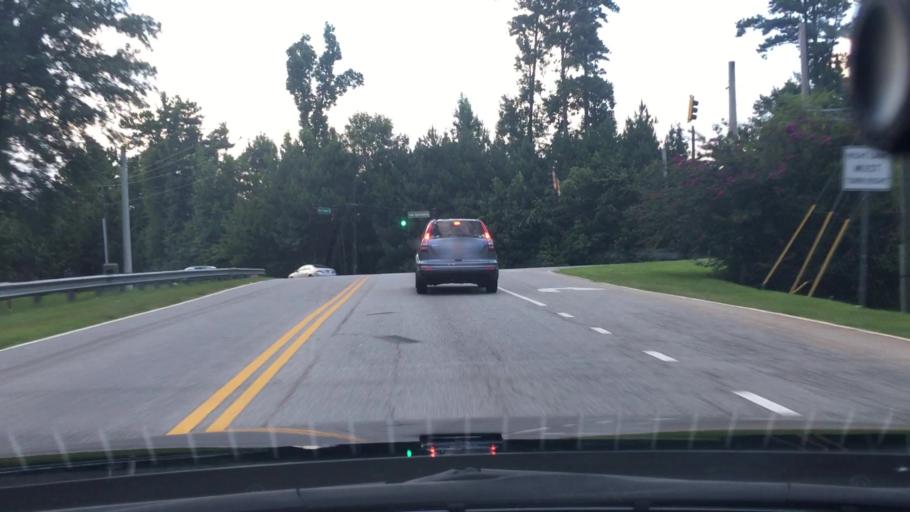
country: US
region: Georgia
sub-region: Coweta County
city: East Newnan
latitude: 33.3729
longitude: -84.7122
